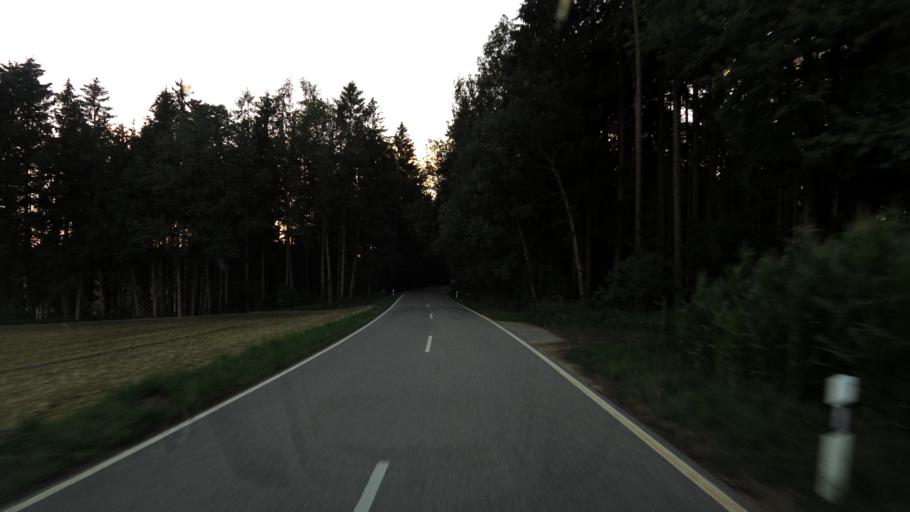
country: DE
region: Bavaria
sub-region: Upper Bavaria
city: Taufkirchen
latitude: 48.1588
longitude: 12.4434
